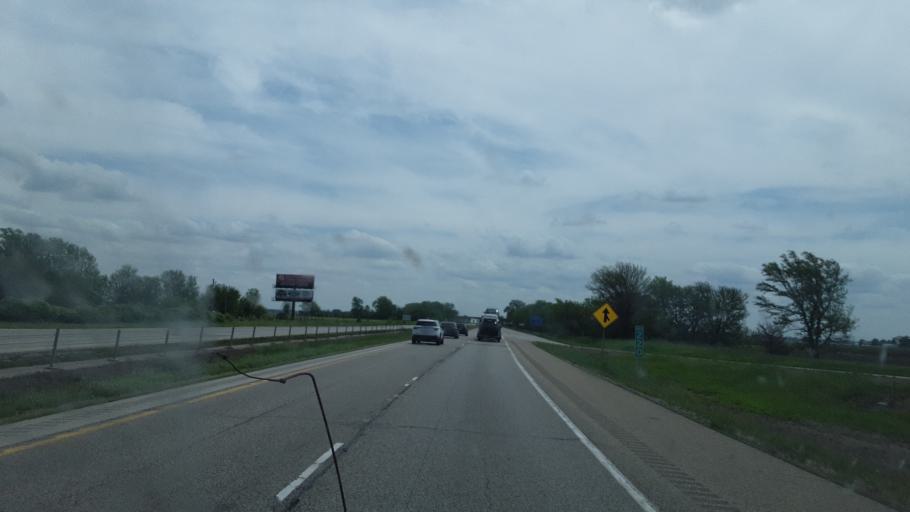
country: US
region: Illinois
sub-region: Vermilion County
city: Danville
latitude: 40.1174
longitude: -87.5327
